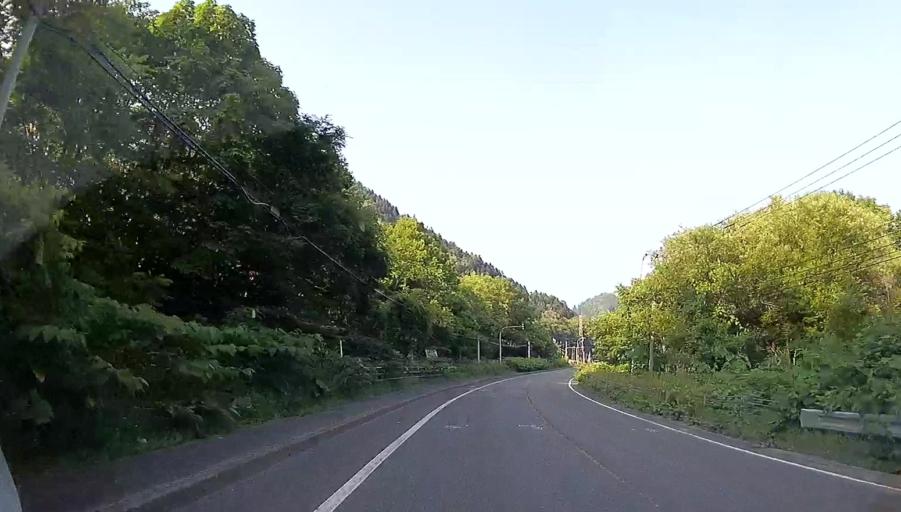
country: JP
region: Hokkaido
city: Shimo-furano
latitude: 42.8931
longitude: 142.4722
